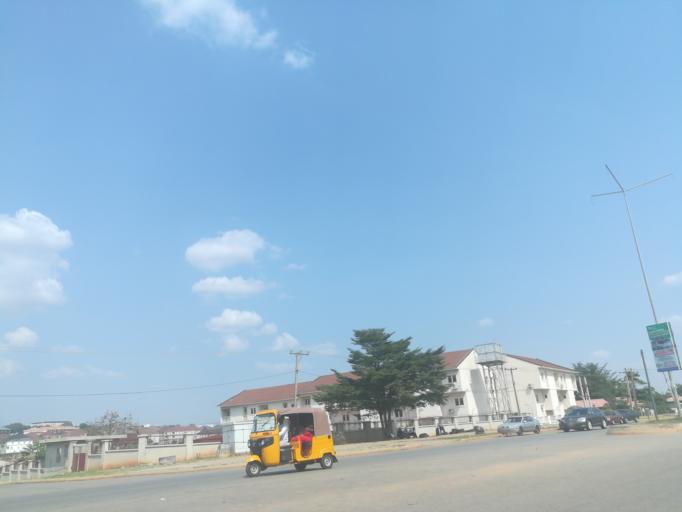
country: NG
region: Abuja Federal Capital Territory
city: Abuja
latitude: 9.0532
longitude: 7.4454
